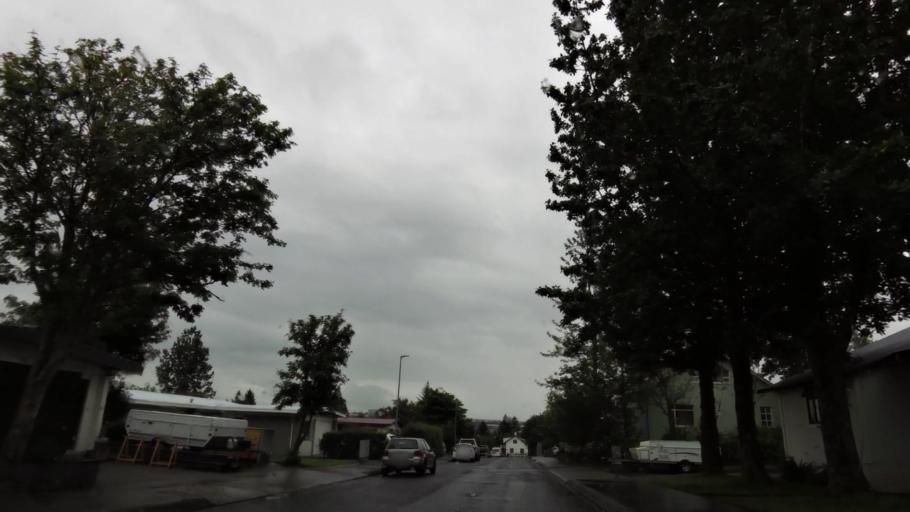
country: IS
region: Capital Region
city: Reykjavik
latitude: 64.1235
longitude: -21.8602
